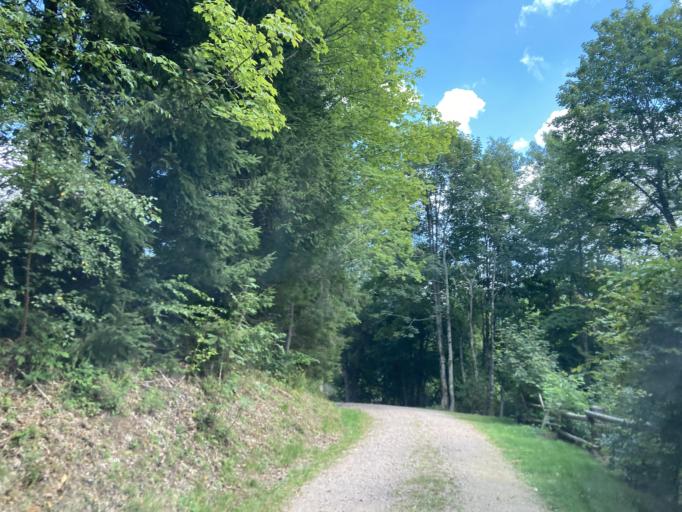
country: DE
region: Baden-Wuerttemberg
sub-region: Freiburg Region
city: Schonach im Schwarzwald
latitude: 48.1490
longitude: 8.1551
